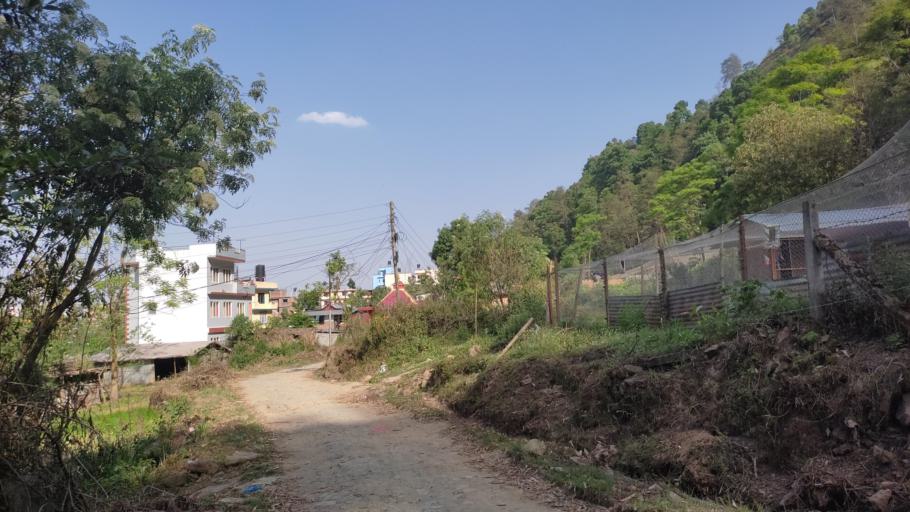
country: NP
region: Central Region
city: Kirtipur
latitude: 27.6571
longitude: 85.2651
